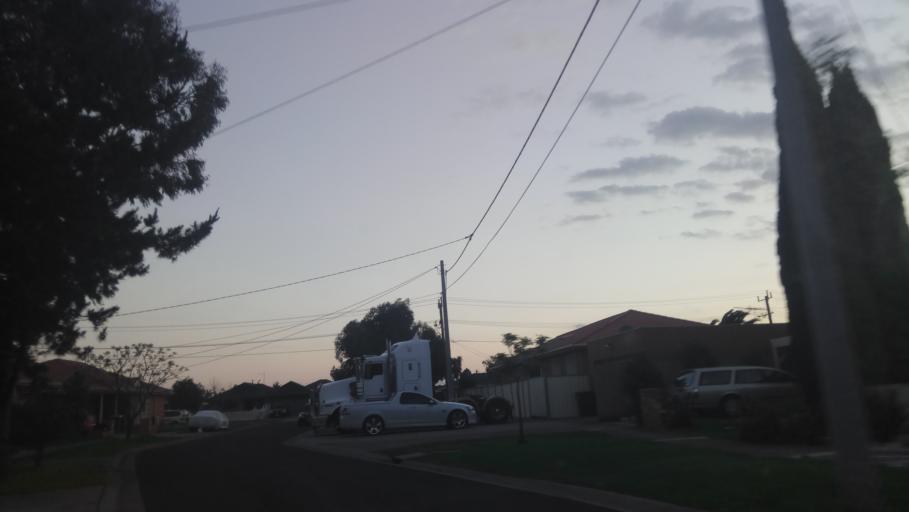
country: AU
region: Victoria
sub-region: Hobsons Bay
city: Altona Meadows
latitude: -37.8816
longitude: 144.7773
